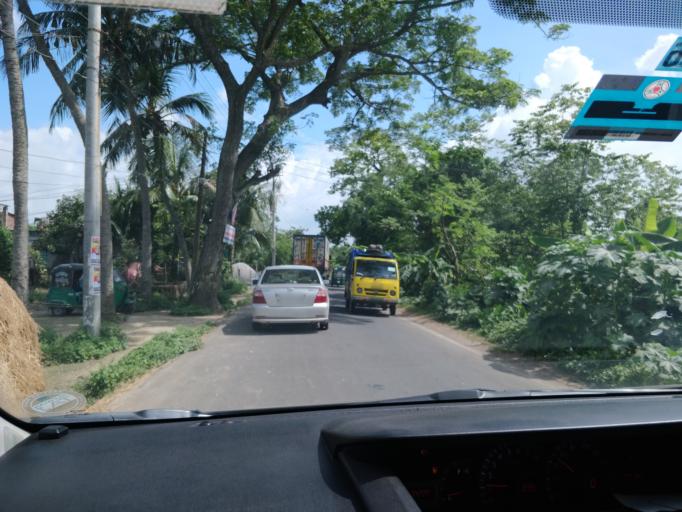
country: BD
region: Dhaka
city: Bhairab Bazar
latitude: 24.1044
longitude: 91.1249
